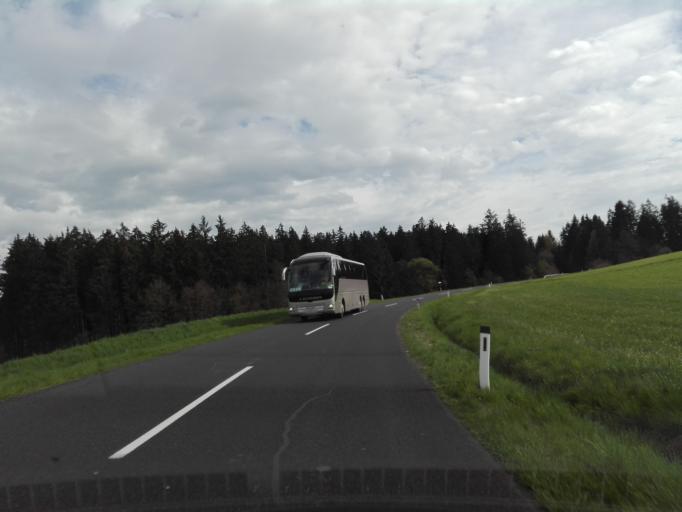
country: AT
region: Upper Austria
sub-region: Politischer Bezirk Rohrbach
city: Kleinzell im Muehlkreis
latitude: 48.4679
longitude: 14.0211
